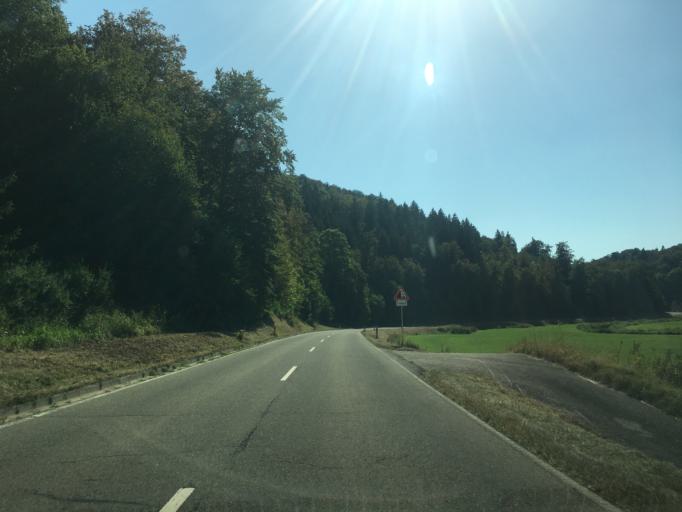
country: DE
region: Baden-Wuerttemberg
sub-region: Tuebingen Region
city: Hayingen
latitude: 48.3142
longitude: 9.5057
